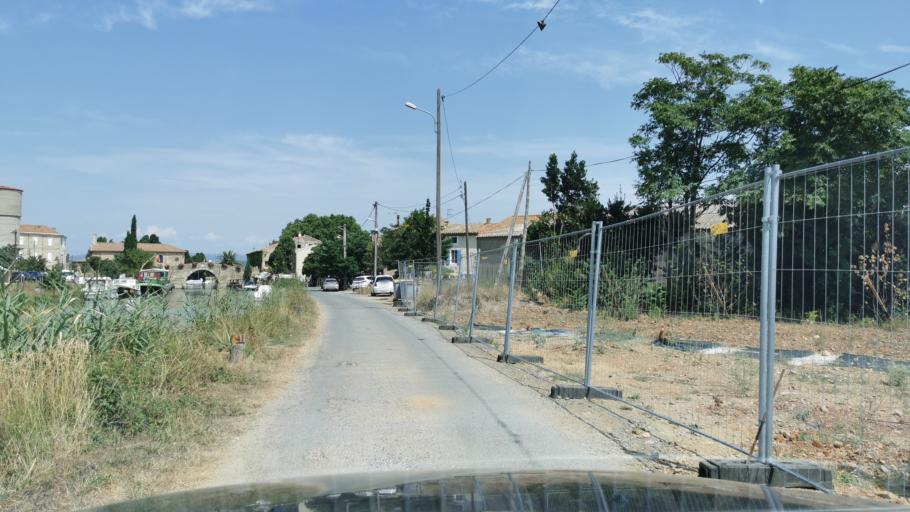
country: FR
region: Languedoc-Roussillon
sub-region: Departement de l'Aude
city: Saint-Marcel-sur-Aude
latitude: 43.2648
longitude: 2.9050
